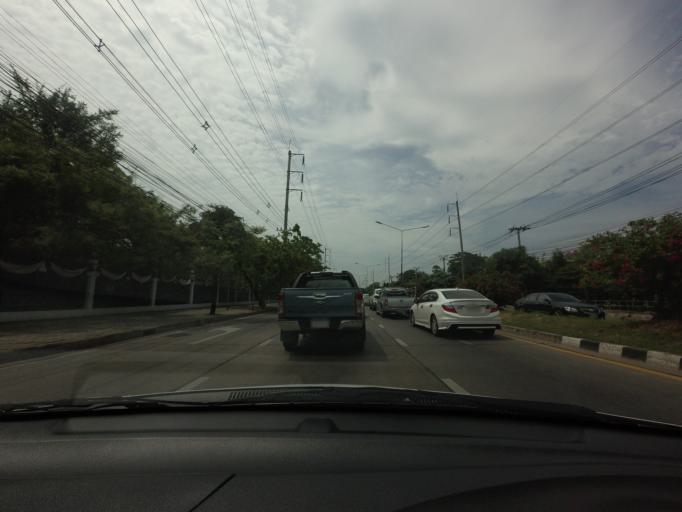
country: TH
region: Nonthaburi
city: Pak Kret
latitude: 13.8953
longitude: 100.5083
